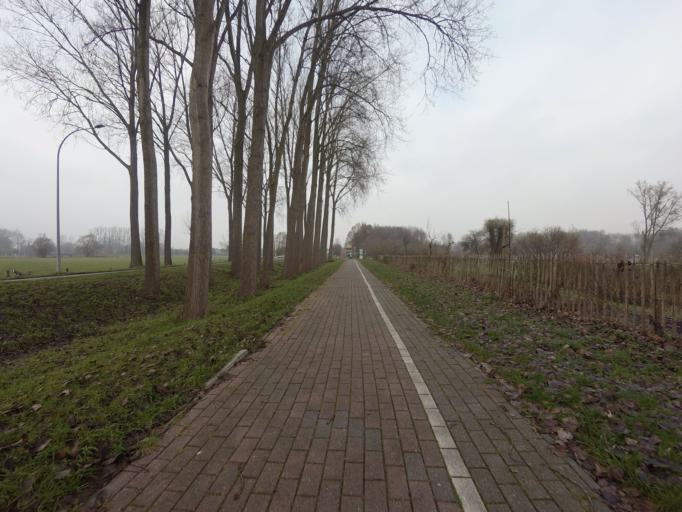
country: BE
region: Flanders
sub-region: Provincie Oost-Vlaanderen
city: Geraardsbergen
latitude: 50.7908
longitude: 3.9045
